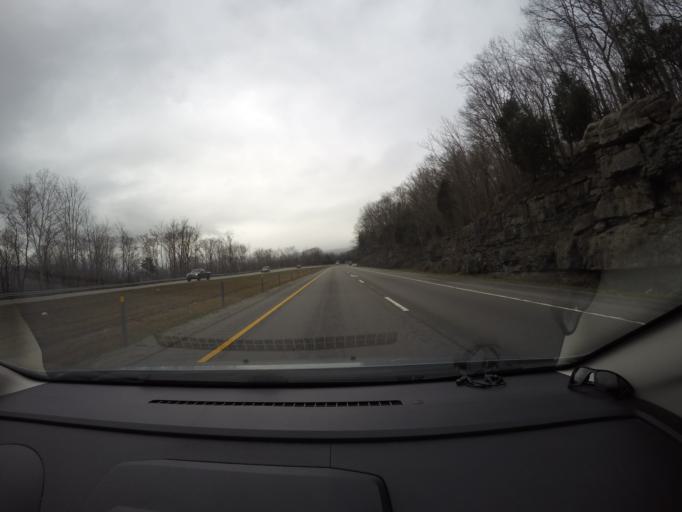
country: US
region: Tennessee
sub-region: Marion County
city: Monteagle
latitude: 35.2675
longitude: -85.8864
